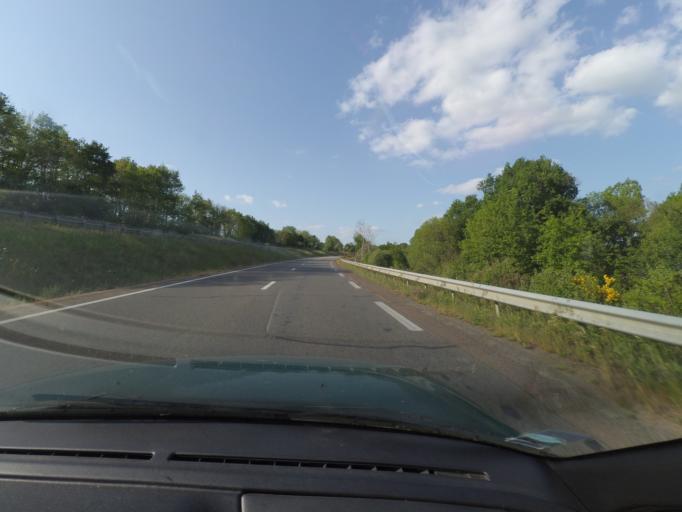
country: FR
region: Pays de la Loire
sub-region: Departement de la Vendee
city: Saligny
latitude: 46.8243
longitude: -1.4286
